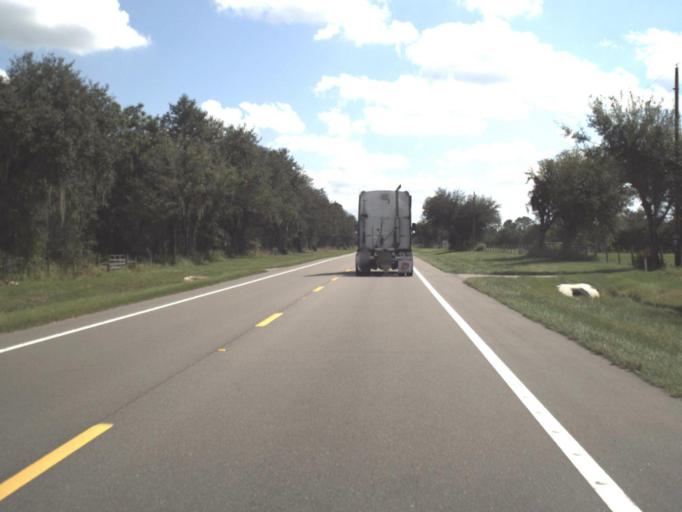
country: US
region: Florida
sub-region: Hardee County
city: Zolfo Springs
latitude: 27.4846
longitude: -81.7358
